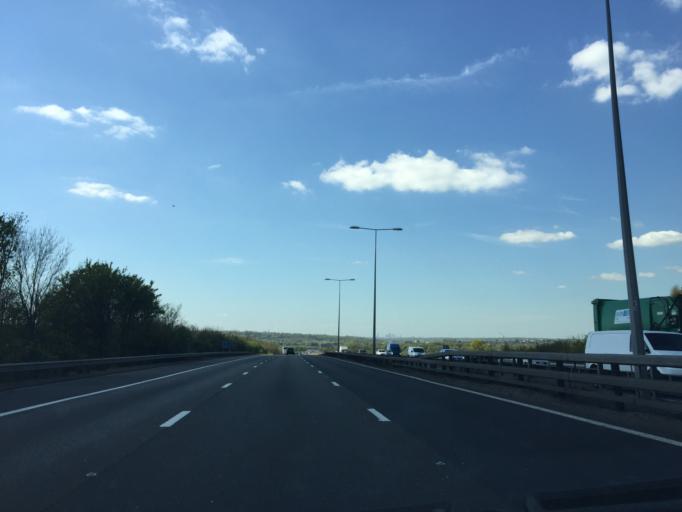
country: GB
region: England
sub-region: Essex
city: Theydon Bois
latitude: 51.6647
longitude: 0.1138
